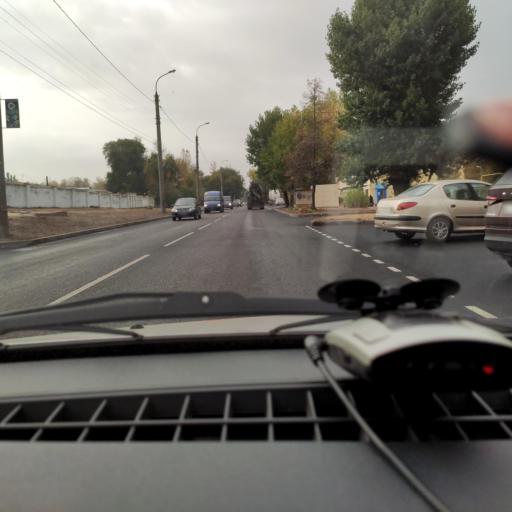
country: RU
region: Voronezj
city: Voronezh
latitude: 51.6456
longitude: 39.2427
